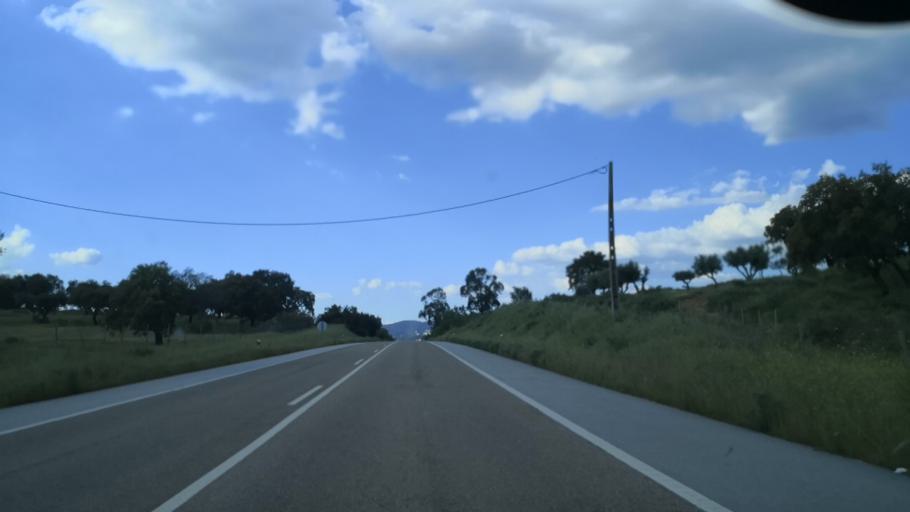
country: PT
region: Portalegre
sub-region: Portalegre
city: Urra
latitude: 39.2370
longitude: -7.4523
